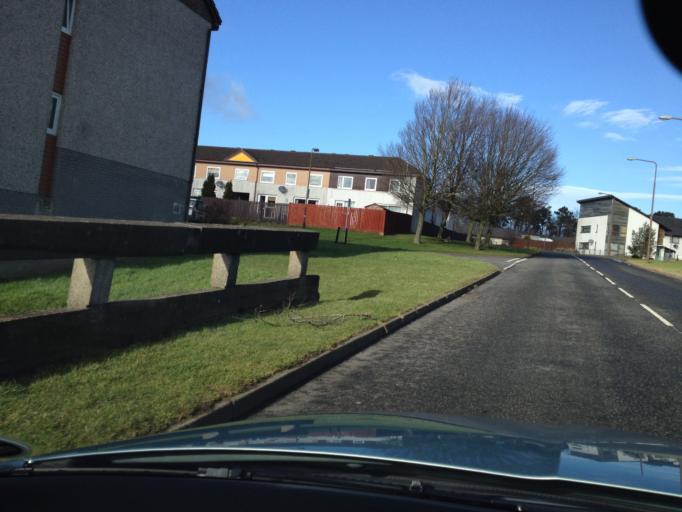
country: GB
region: Scotland
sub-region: West Lothian
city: Mid Calder
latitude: 55.9017
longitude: -3.4924
